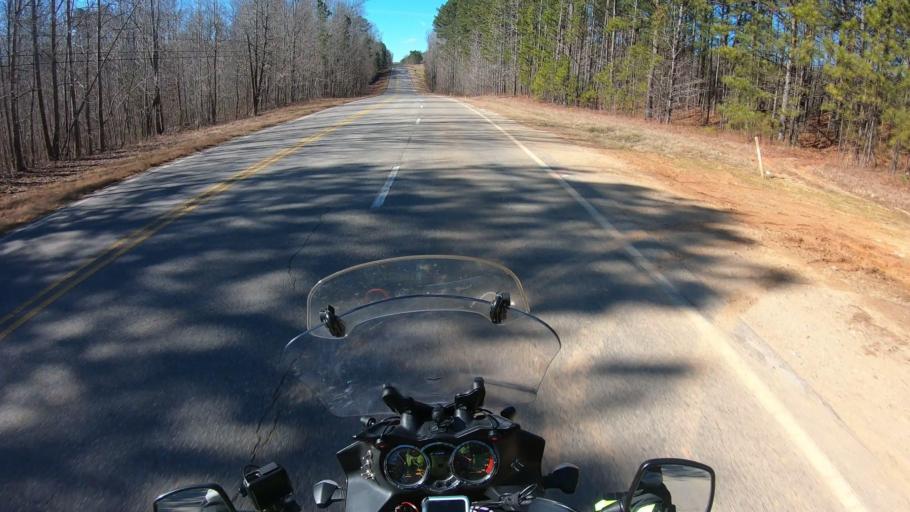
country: US
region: Georgia
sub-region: Haralson County
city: Tallapoosa
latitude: 33.7491
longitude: -85.3621
